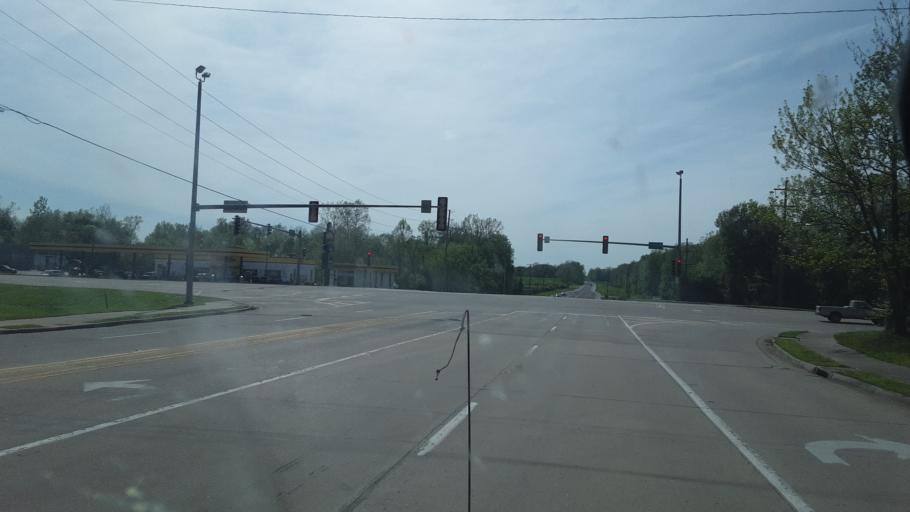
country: US
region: Illinois
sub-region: Jackson County
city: Carbondale
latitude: 37.7004
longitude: -89.2180
